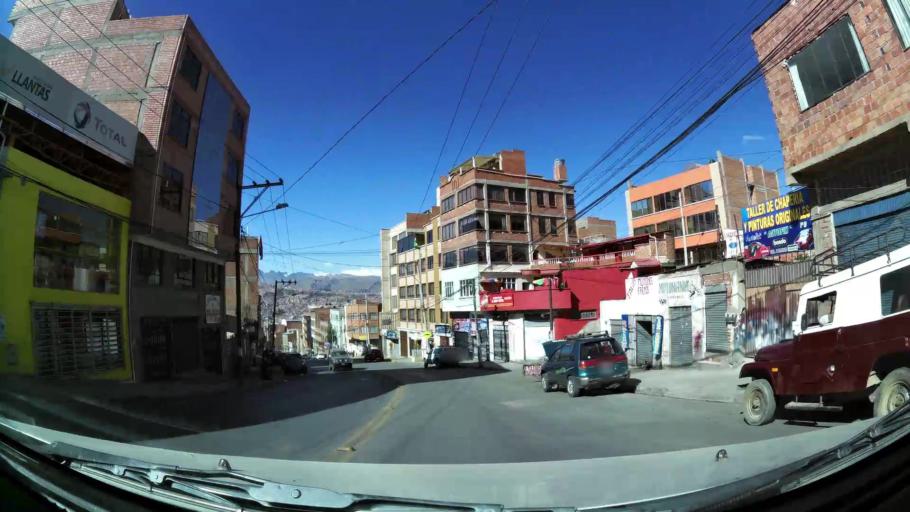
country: BO
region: La Paz
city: La Paz
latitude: -16.5116
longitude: -68.1395
